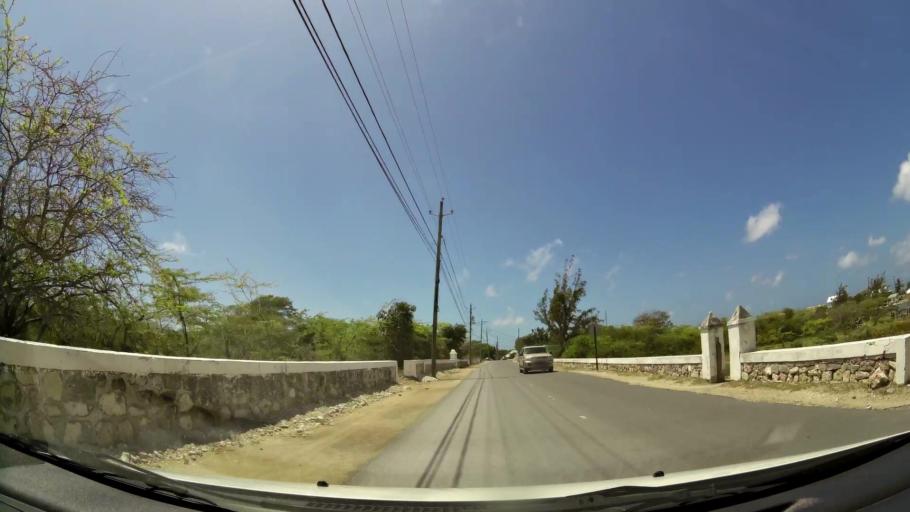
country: TC
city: Cockburn Town
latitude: 21.4756
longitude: -71.1458
